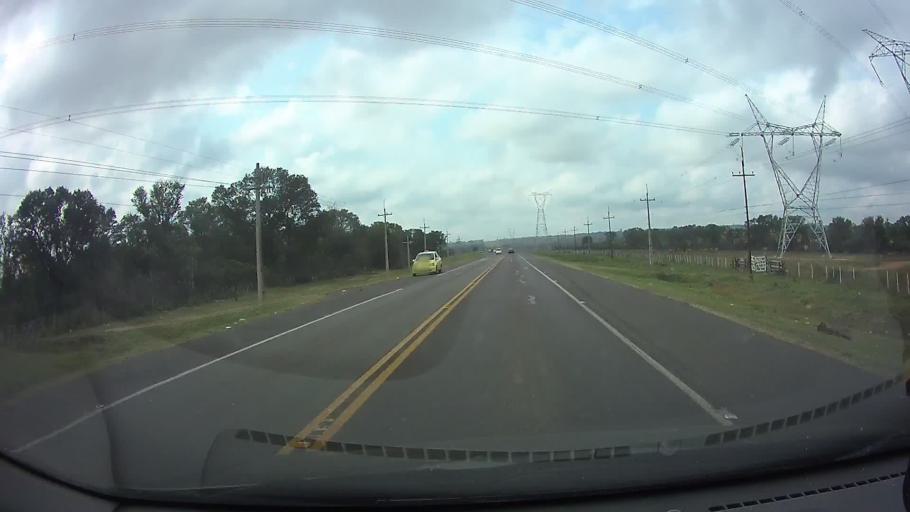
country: PY
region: Central
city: Limpio
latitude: -25.1146
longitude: -57.4232
